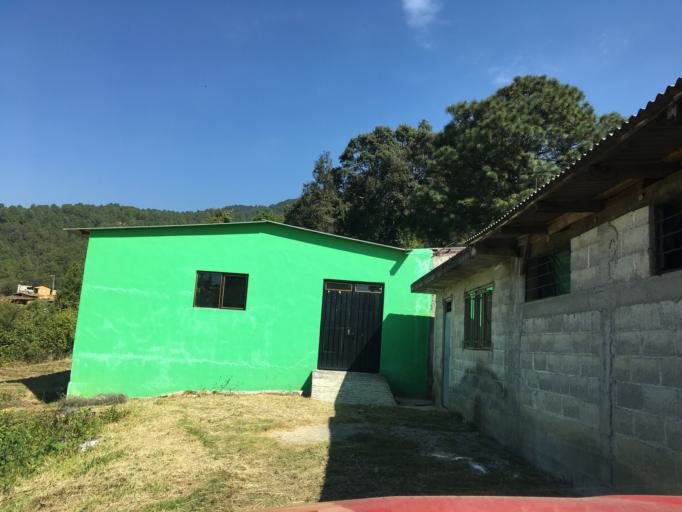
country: MX
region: Michoacan
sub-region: Zitacuaro
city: Macutzio
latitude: 19.4946
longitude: -100.3231
